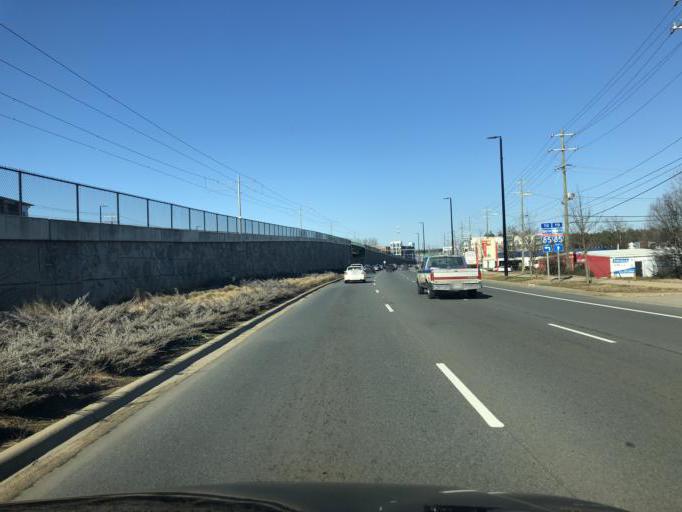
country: US
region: North Carolina
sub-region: Mecklenburg County
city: Charlotte
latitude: 35.2822
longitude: -80.7647
